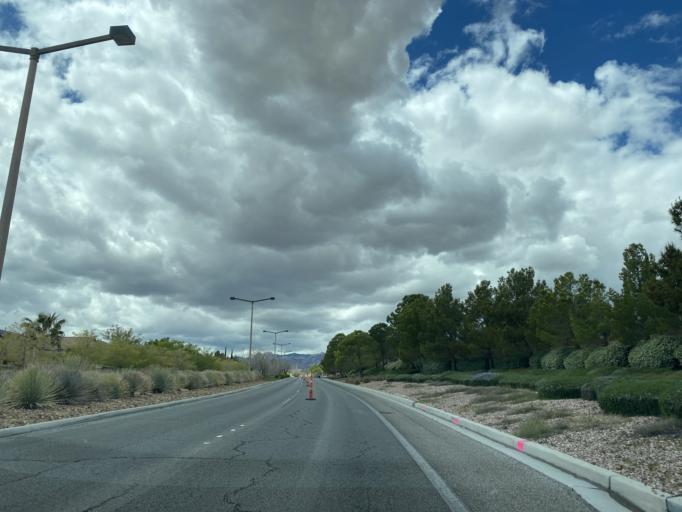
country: US
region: Nevada
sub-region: Clark County
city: Summerlin South
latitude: 36.1728
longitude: -115.3490
